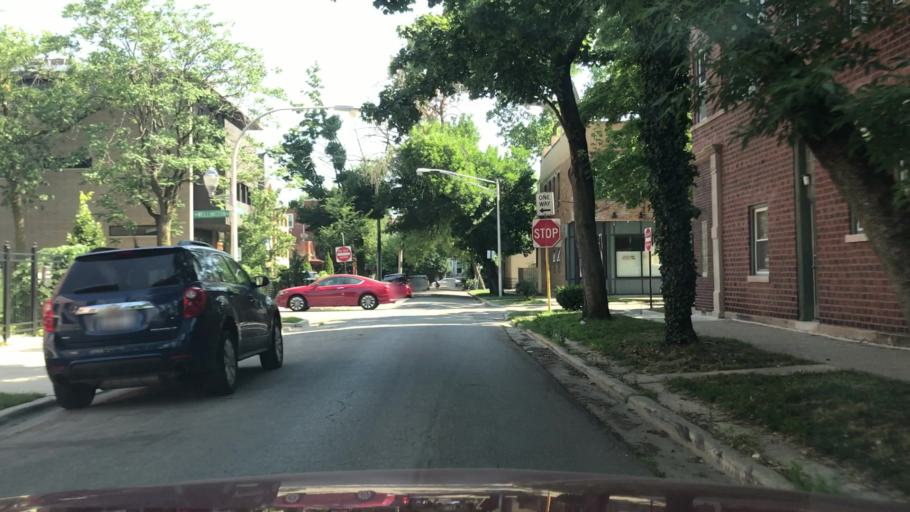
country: US
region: Illinois
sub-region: Cook County
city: Lincolnwood
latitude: 41.9364
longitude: -87.6742
